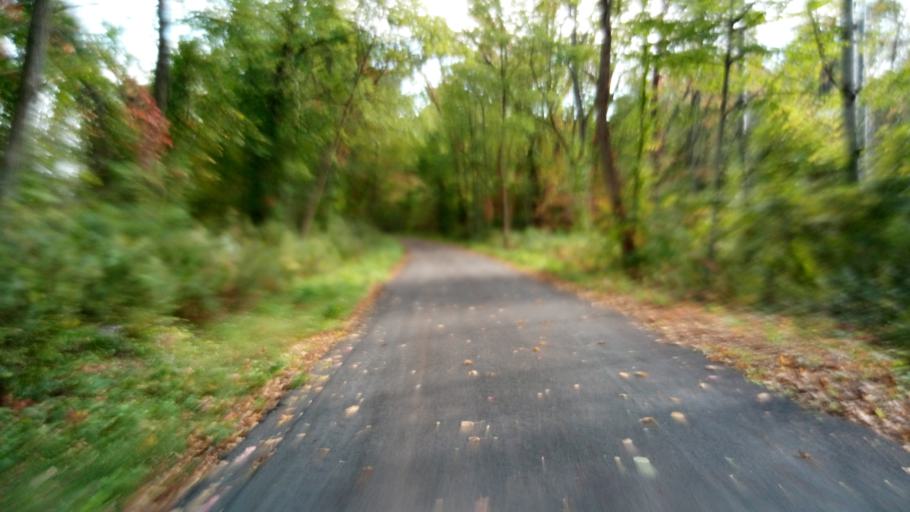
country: US
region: New York
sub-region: Wayne County
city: Clyde
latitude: 43.0691
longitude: -76.8556
